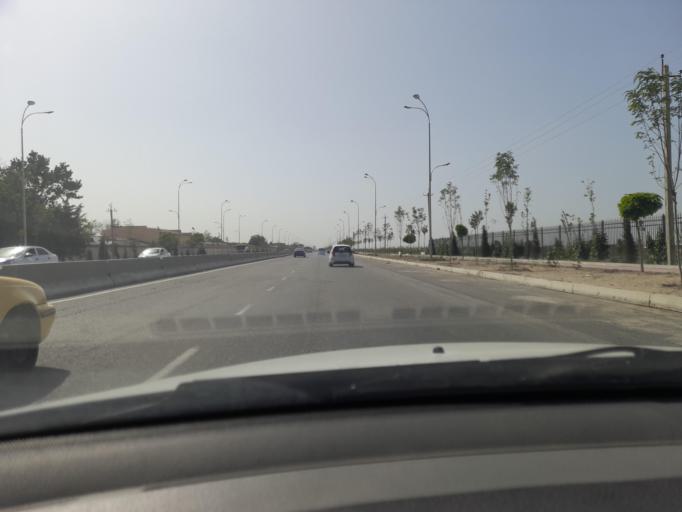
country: UZ
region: Samarqand
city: Samarqand
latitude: 39.7071
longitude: 66.9914
